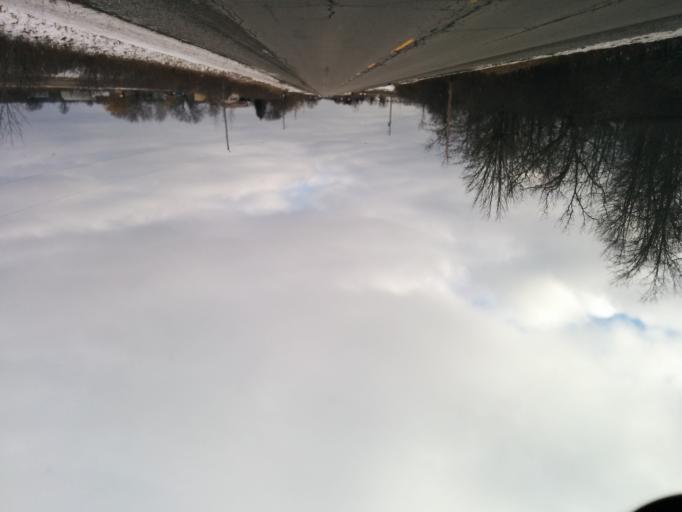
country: CA
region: Ontario
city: Brantford
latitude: 42.9843
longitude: -80.1122
